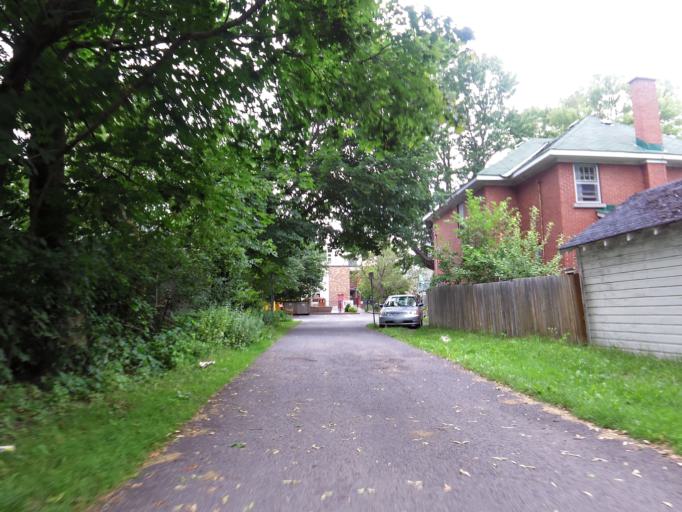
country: CA
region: Ontario
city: Ottawa
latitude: 45.3969
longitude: -75.7250
